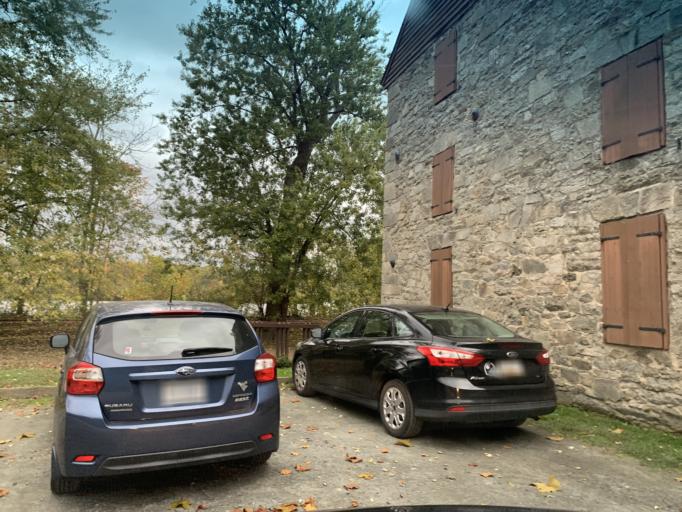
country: US
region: Maryland
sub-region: Harford County
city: Havre de Grace
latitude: 39.6080
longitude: -76.1424
